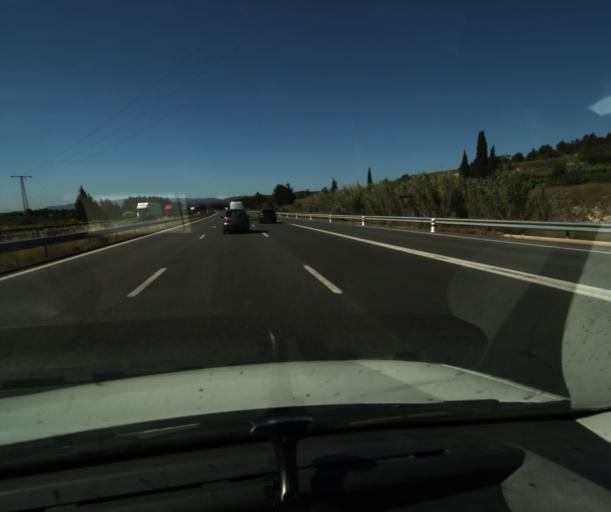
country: FR
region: Languedoc-Roussillon
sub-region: Departement de l'Aude
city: Peyriac-de-Mer
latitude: 43.1118
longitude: 2.9519
